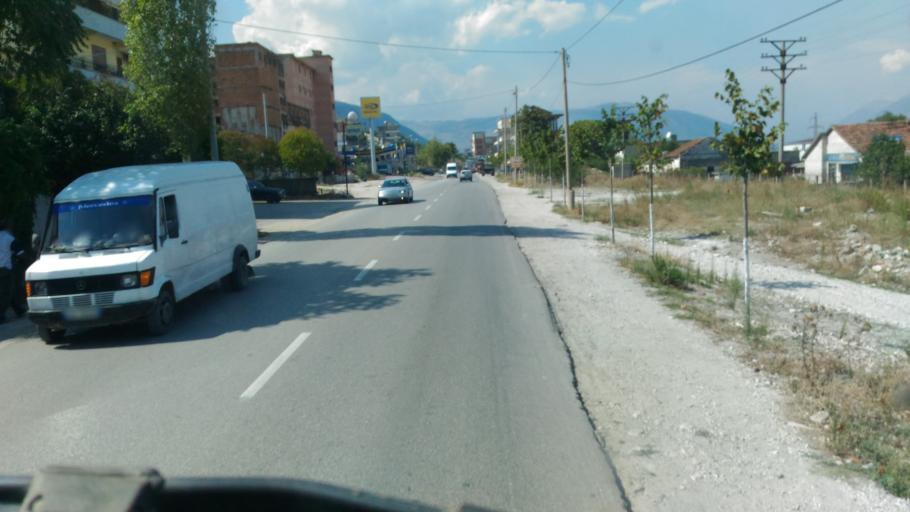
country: AL
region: Gjirokaster
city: Gjirokaster
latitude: 40.0727
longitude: 20.1568
